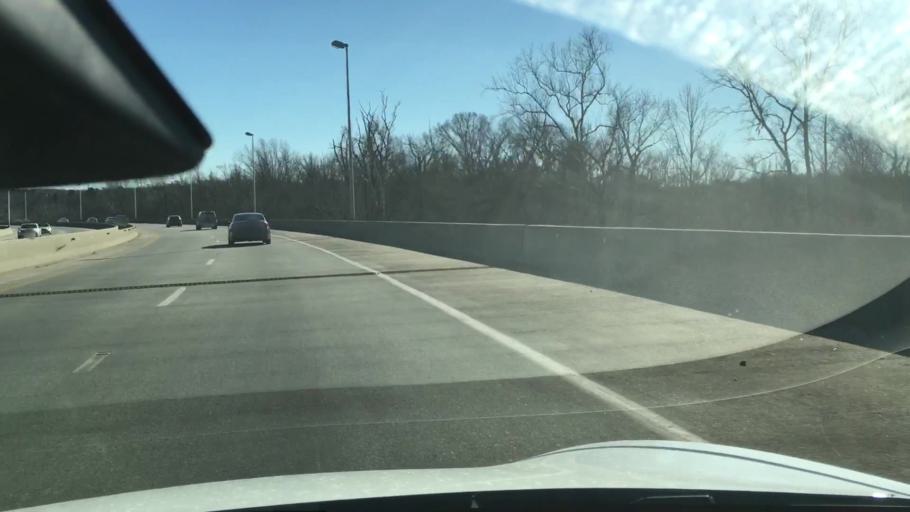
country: US
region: Virginia
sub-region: Henrico County
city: Tuckahoe
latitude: 37.5645
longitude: -77.5772
